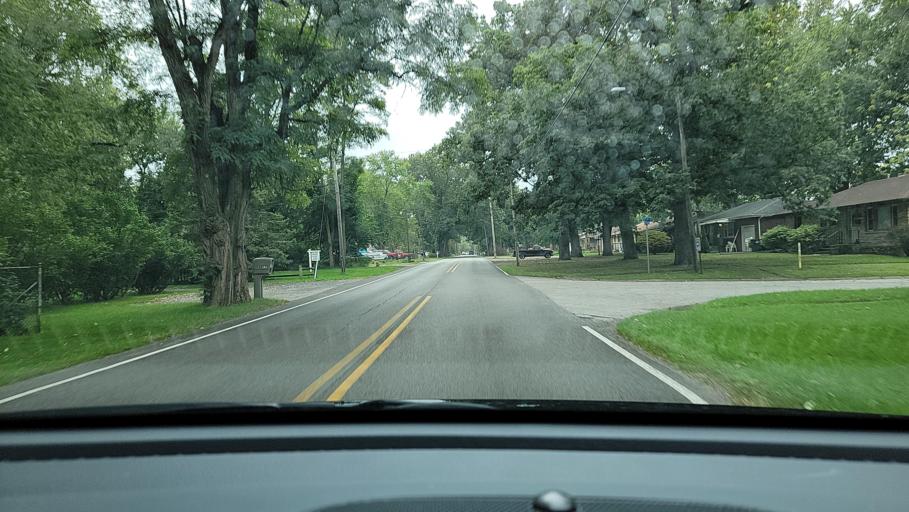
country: US
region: Indiana
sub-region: Lake County
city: Lake Station
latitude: 41.5689
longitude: -87.2219
